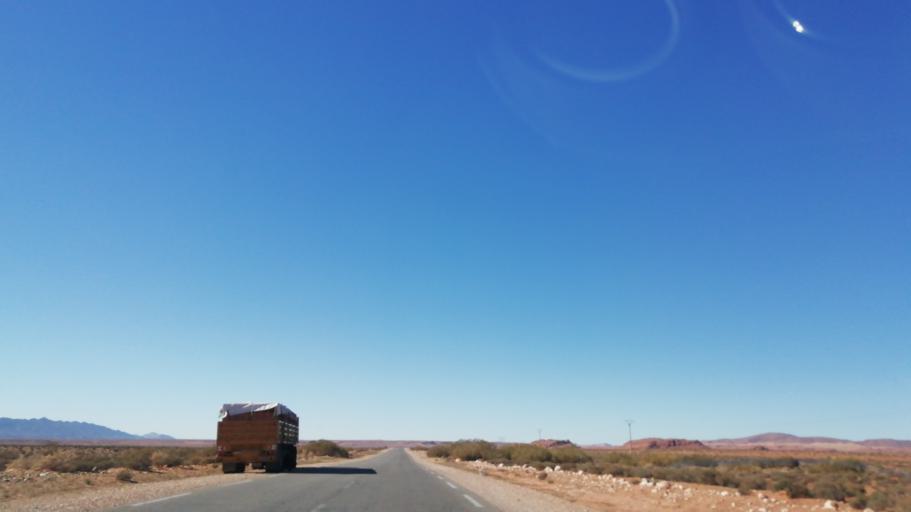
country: DZ
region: El Bayadh
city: El Abiodh Sidi Cheikh
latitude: 33.1810
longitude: 0.5475
